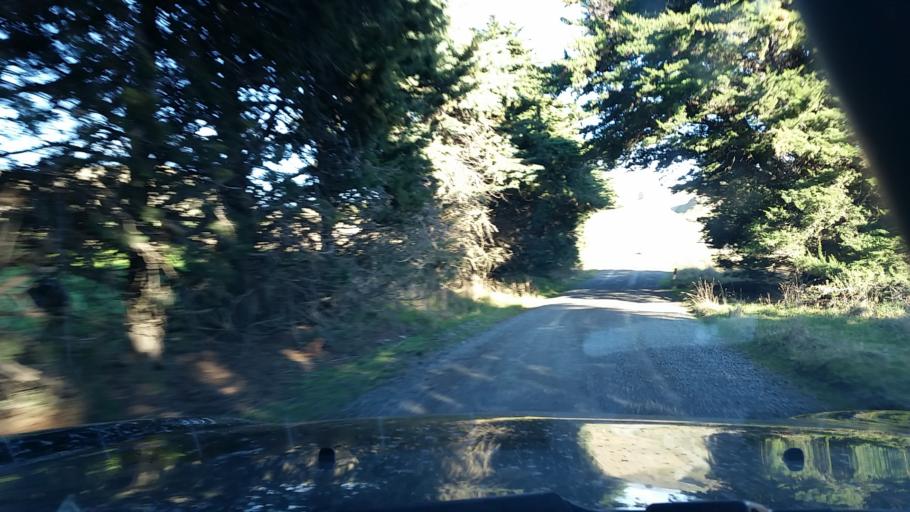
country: NZ
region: Marlborough
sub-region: Marlborough District
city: Blenheim
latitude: -41.7359
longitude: 173.9964
